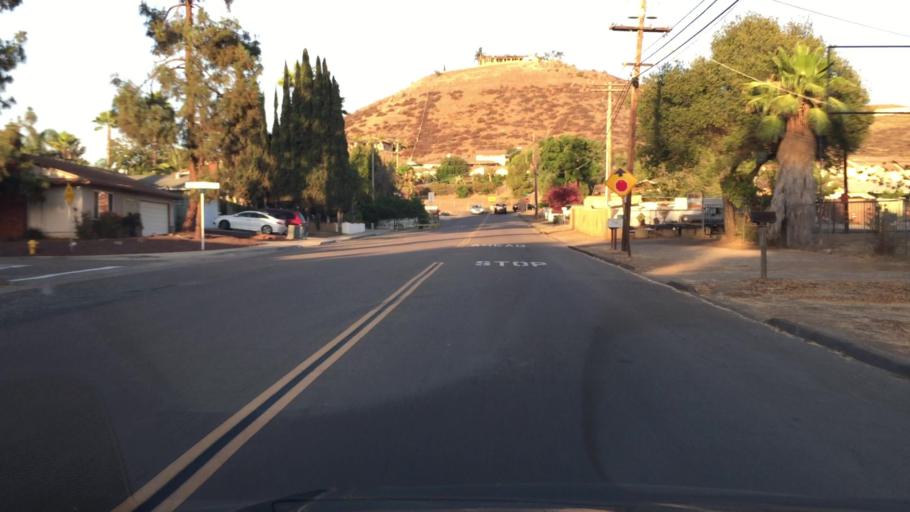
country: US
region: California
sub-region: San Diego County
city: Bostonia
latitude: 32.8191
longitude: -116.9462
